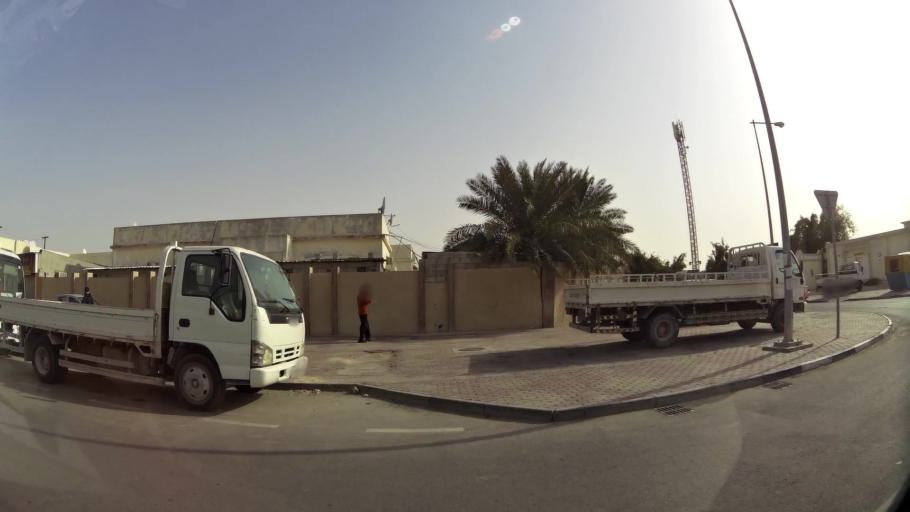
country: QA
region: Baladiyat ar Rayyan
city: Ar Rayyan
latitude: 25.2358
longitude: 51.4345
